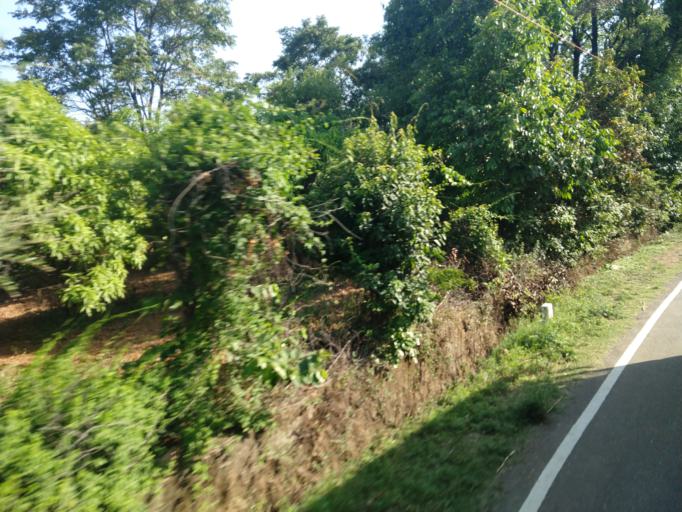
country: IN
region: Himachal Pradesh
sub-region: Chamba
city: Chowari
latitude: 32.3742
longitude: 75.9259
